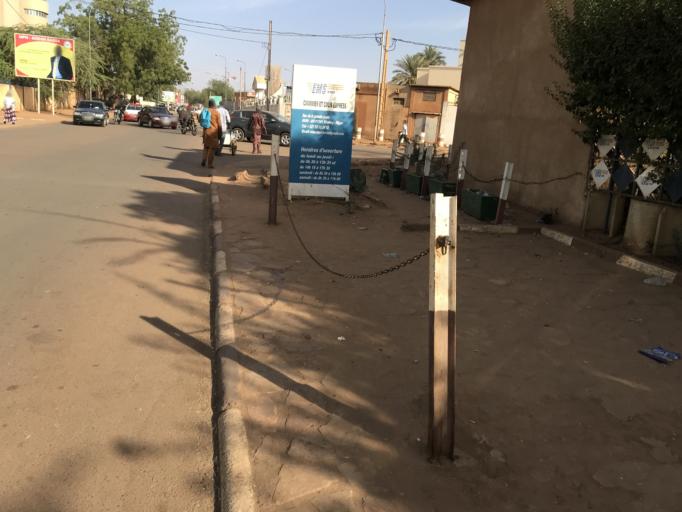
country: NE
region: Niamey
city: Niamey
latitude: 13.5104
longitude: 2.1143
